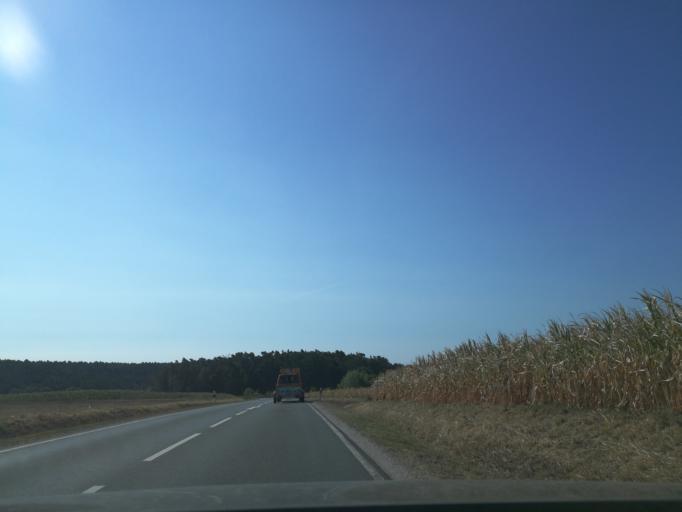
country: DE
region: Bavaria
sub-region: Regierungsbezirk Mittelfranken
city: Ammerndorf
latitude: 49.4390
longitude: 10.8512
